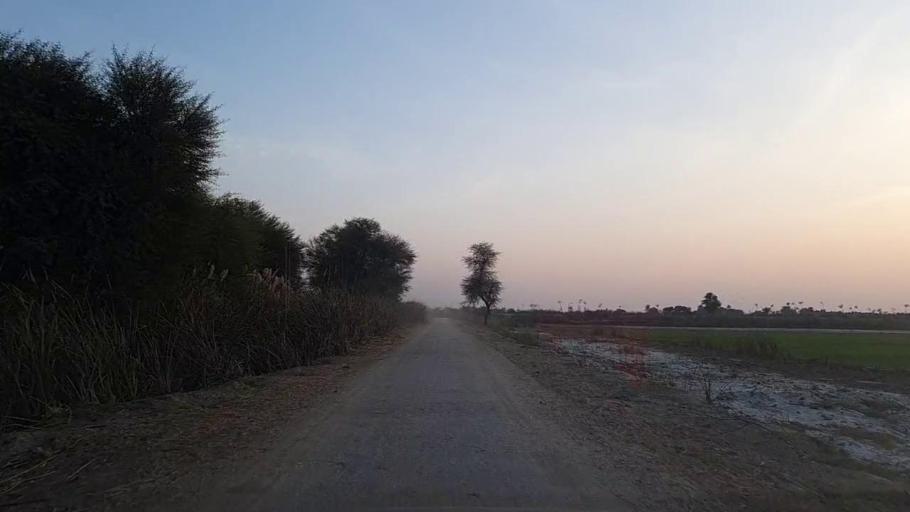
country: PK
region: Sindh
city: Tando Mittha Khan
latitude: 25.9496
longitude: 69.1164
